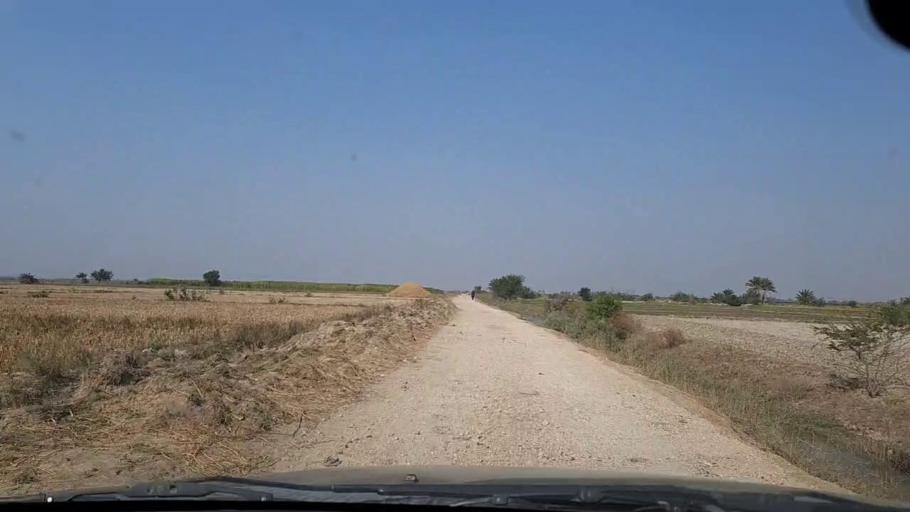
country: PK
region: Sindh
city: Mirpur Sakro
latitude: 24.3631
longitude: 67.6830
